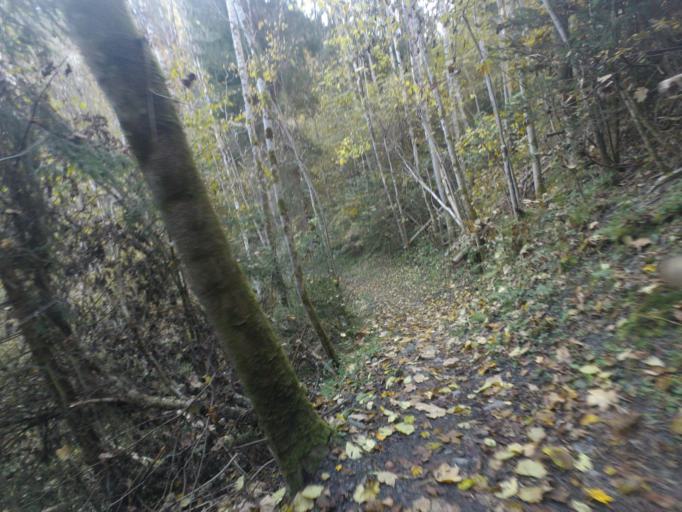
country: AT
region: Salzburg
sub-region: Politischer Bezirk Sankt Johann im Pongau
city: Schwarzach im Pongau
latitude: 47.3139
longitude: 13.1887
